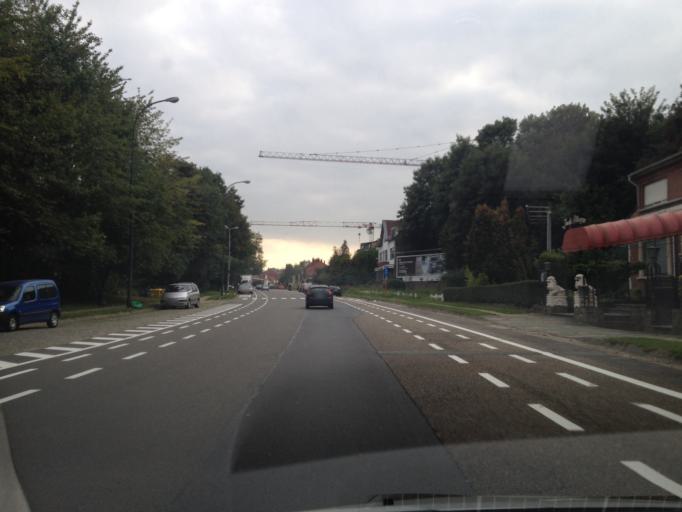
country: BE
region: Flanders
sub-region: Provincie Vlaams-Brabant
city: Bever
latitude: 50.8979
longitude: 4.3232
